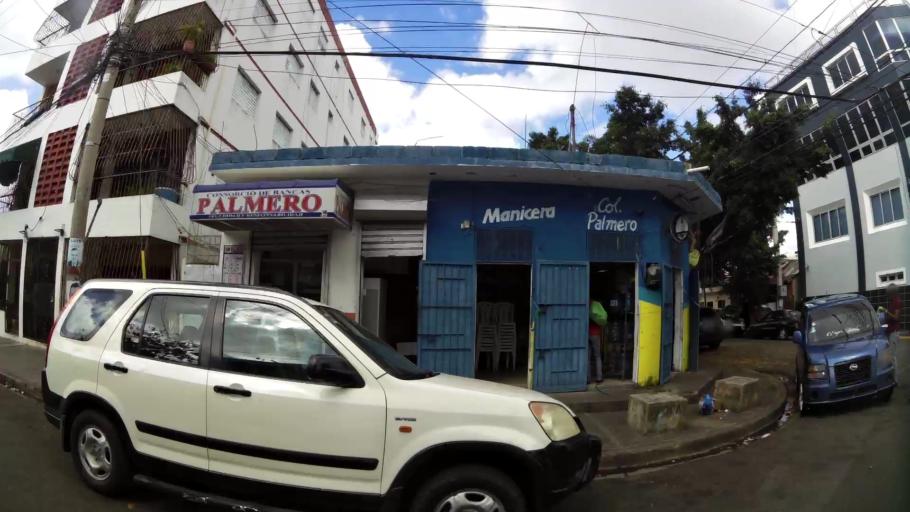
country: DO
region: Nacional
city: San Carlos
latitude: 18.4841
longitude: -69.8970
